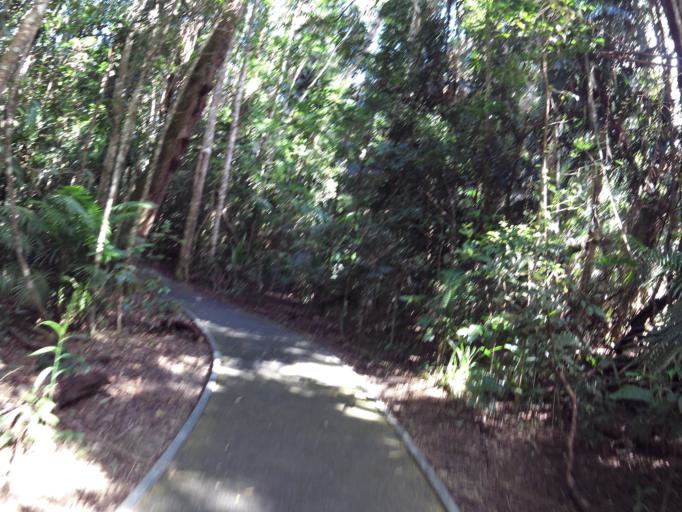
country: AU
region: Queensland
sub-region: Tablelands
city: Kuranda
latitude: -16.8244
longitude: 145.6335
